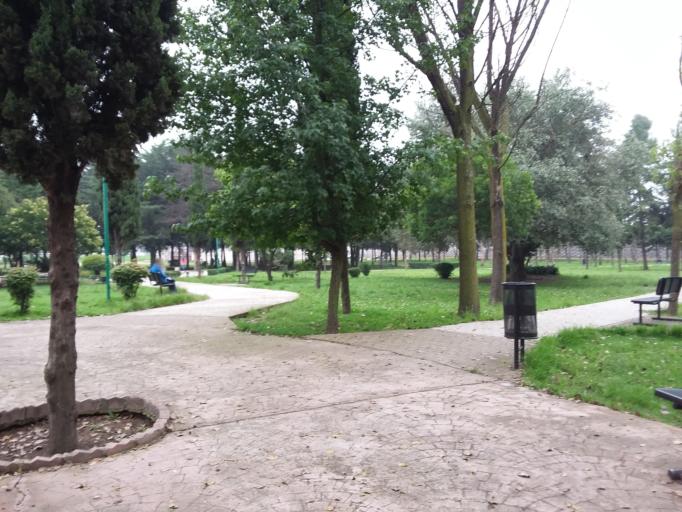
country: MX
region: Mexico
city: Toluca
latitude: 19.3164
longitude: -99.6492
